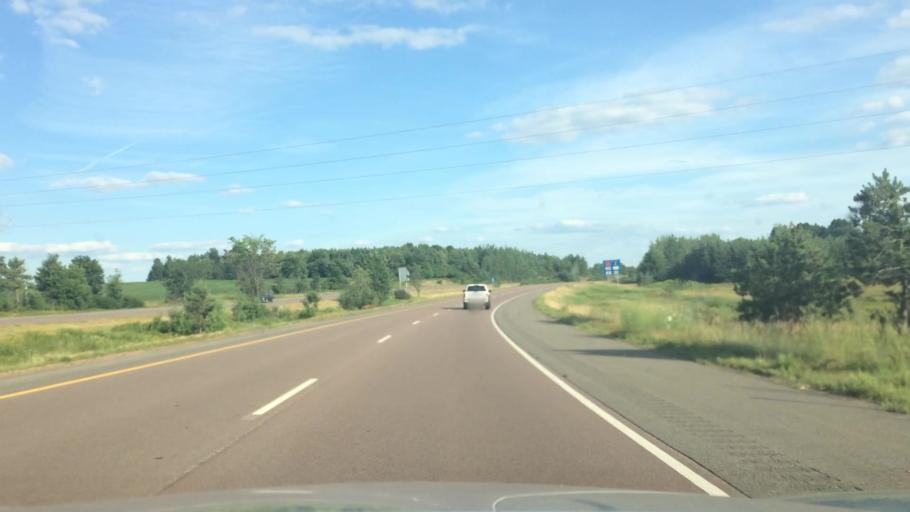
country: US
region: Wisconsin
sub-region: Marathon County
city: Wausau
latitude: 45.0104
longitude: -89.6620
